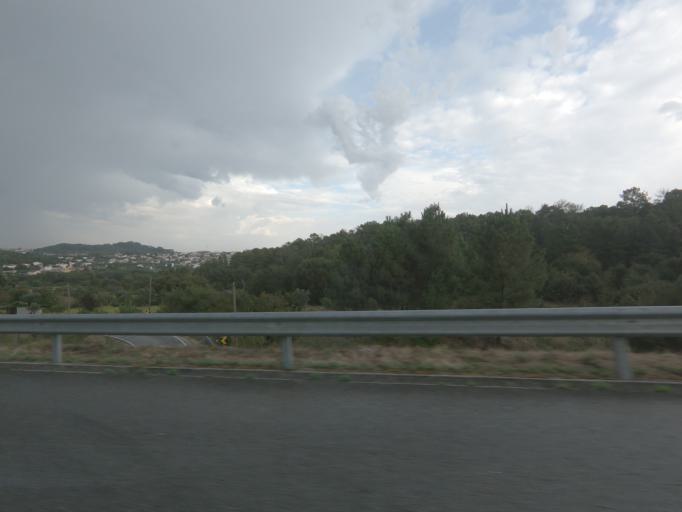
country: PT
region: Viseu
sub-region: Viseu
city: Abraveses
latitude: 40.6995
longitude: -7.9558
